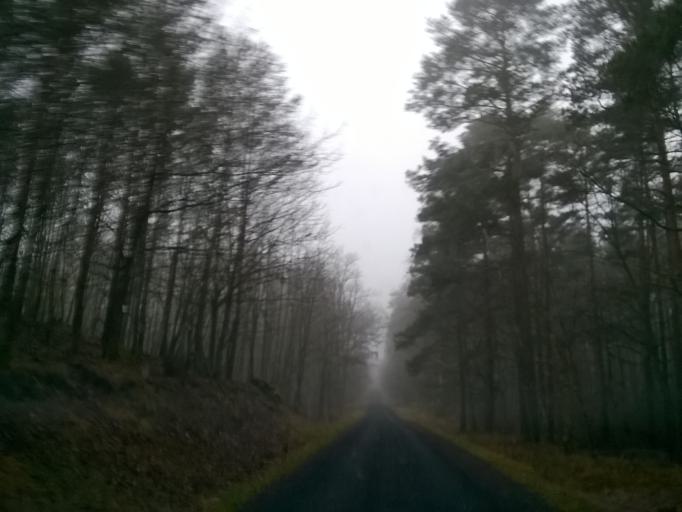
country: PL
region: Kujawsko-Pomorskie
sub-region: Powiat nakielski
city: Kcynia
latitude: 53.0463
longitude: 17.4961
